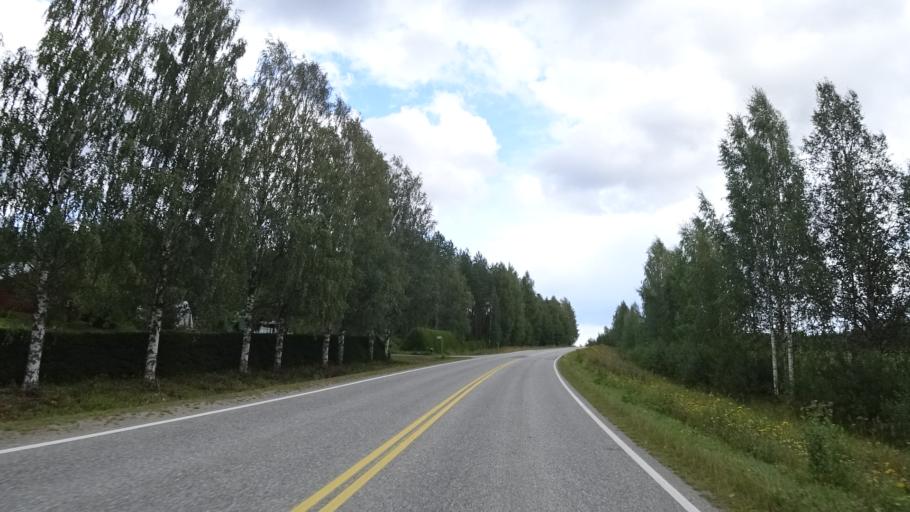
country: FI
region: North Karelia
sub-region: Joensuu
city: Ilomantsi
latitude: 62.6494
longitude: 30.9890
